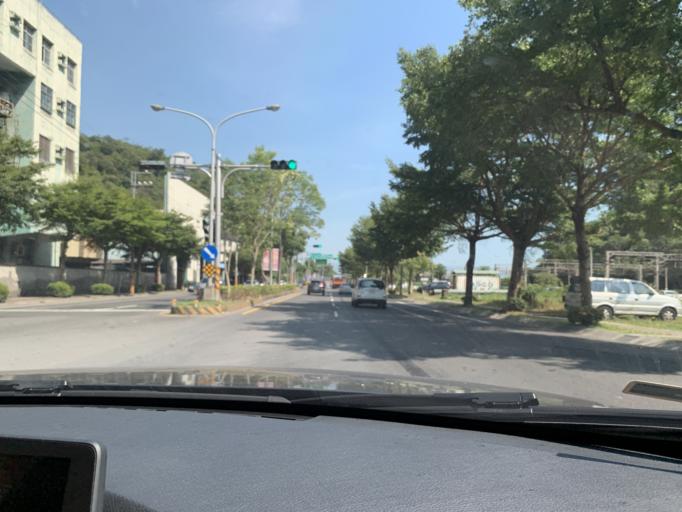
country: TW
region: Taiwan
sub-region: Yilan
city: Yilan
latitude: 24.6095
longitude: 121.8264
